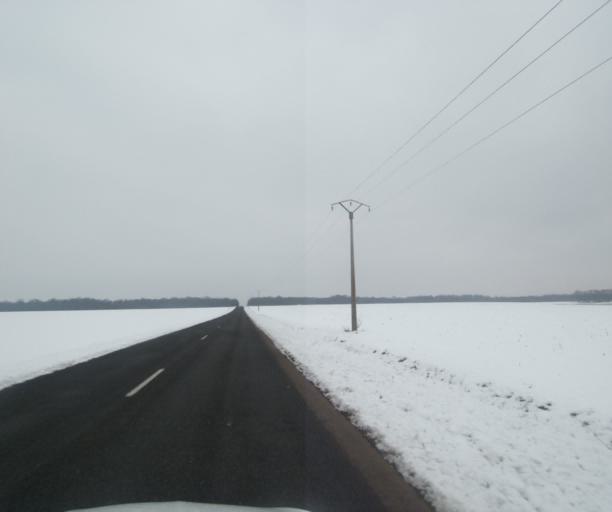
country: FR
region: Champagne-Ardenne
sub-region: Departement de la Haute-Marne
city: Villiers-en-Lieu
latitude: 48.6027
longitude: 4.8780
